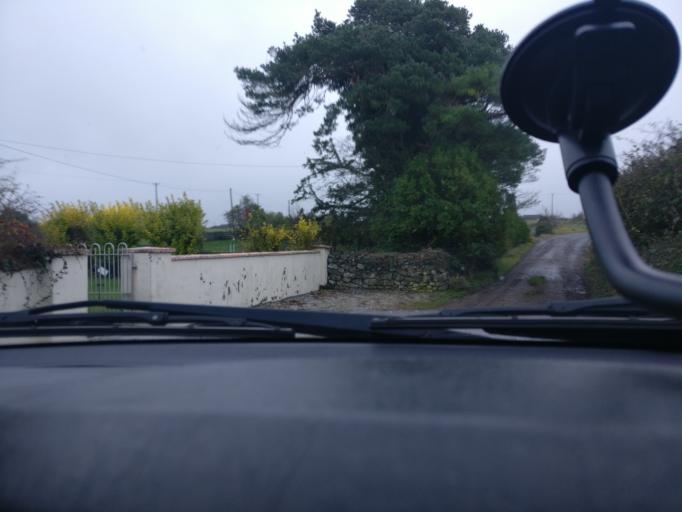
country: IE
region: Connaught
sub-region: County Galway
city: Loughrea
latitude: 53.2074
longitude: -8.5469
